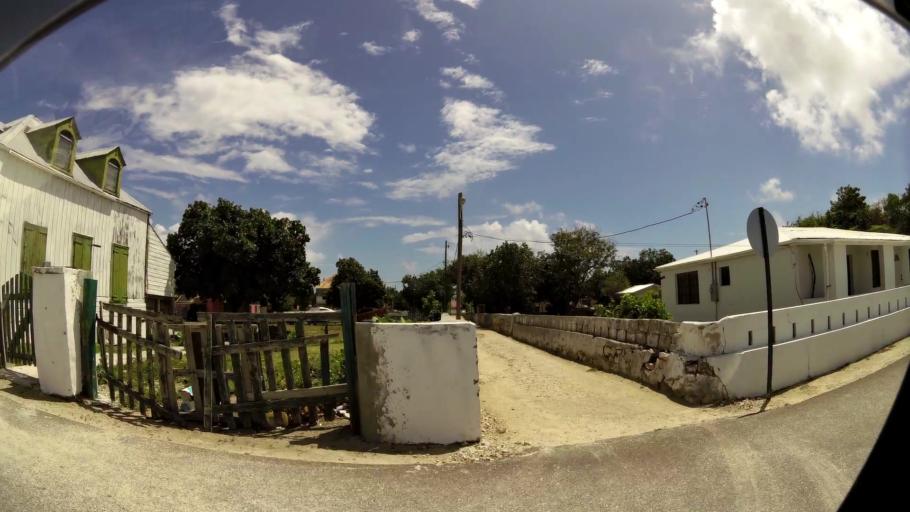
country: TC
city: Cockburn Town
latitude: 21.4718
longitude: -71.1476
